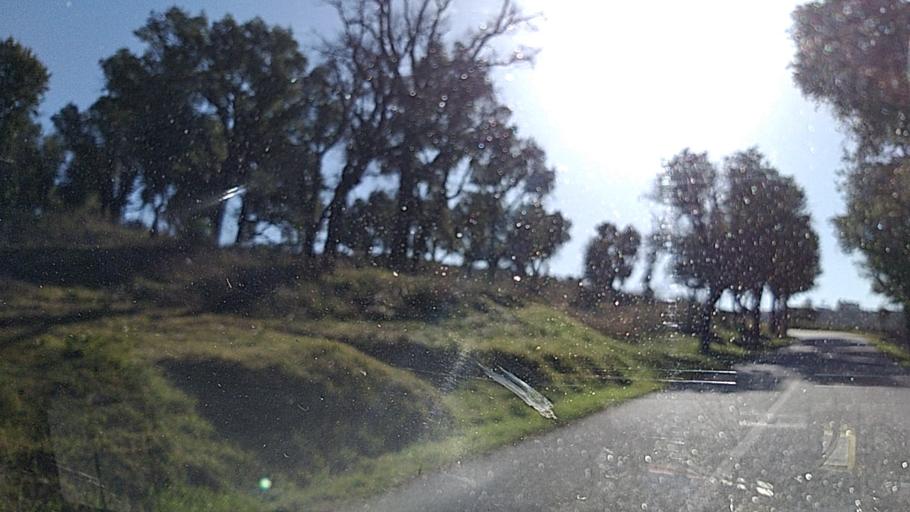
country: PT
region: Guarda
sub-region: Celorico da Beira
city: Celorico da Beira
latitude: 40.6940
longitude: -7.4495
